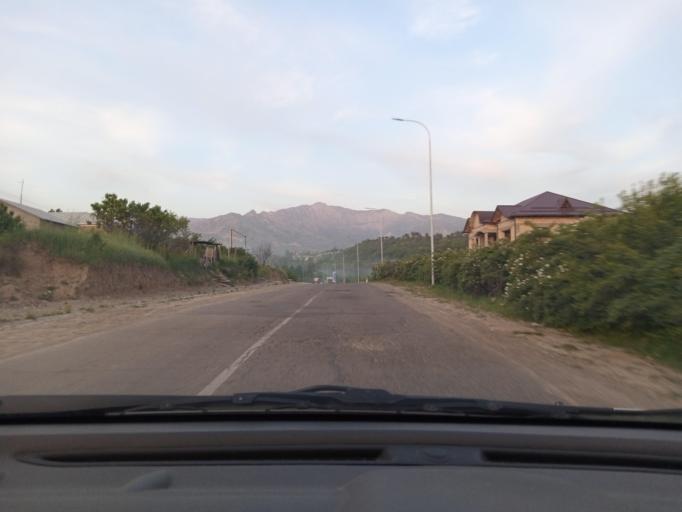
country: UZ
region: Toshkent
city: Parkent
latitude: 41.2452
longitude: 69.7475
